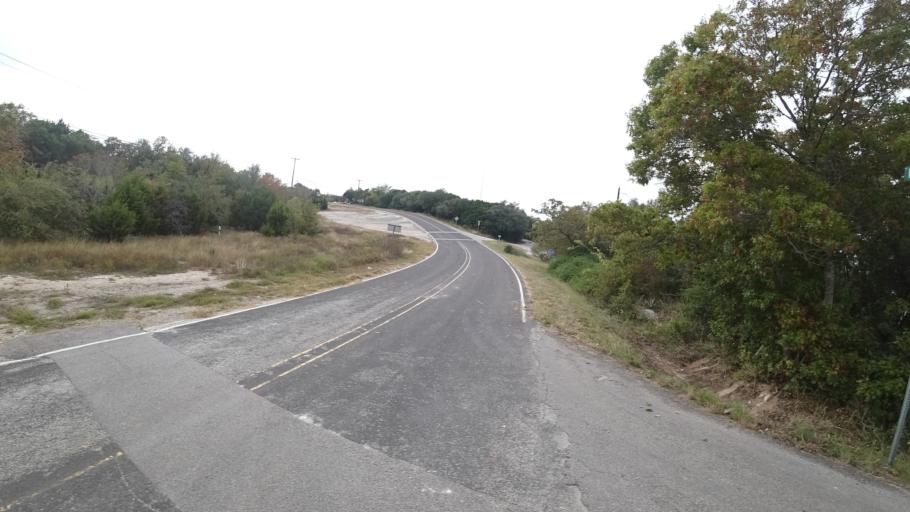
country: US
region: Texas
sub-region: Travis County
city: Hudson Bend
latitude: 30.3933
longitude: -97.8863
